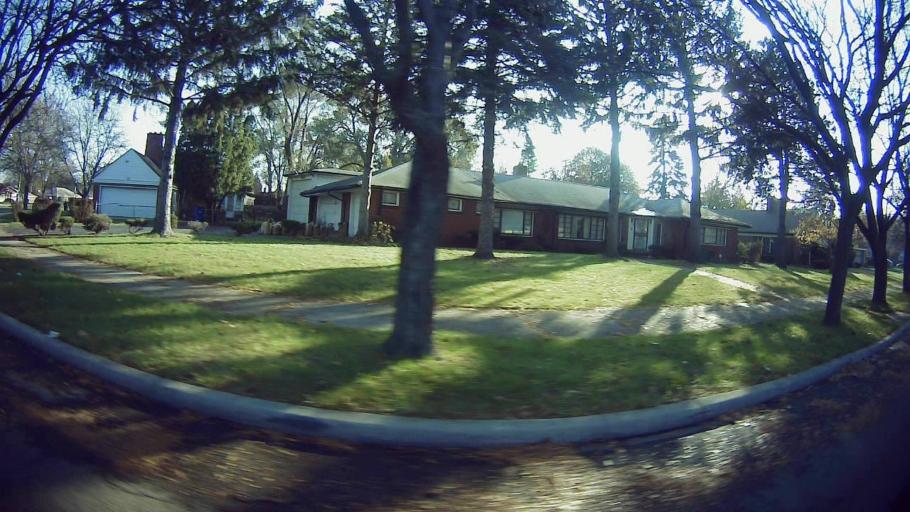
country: US
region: Michigan
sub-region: Wayne County
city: Dearborn
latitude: 42.3558
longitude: -83.1699
